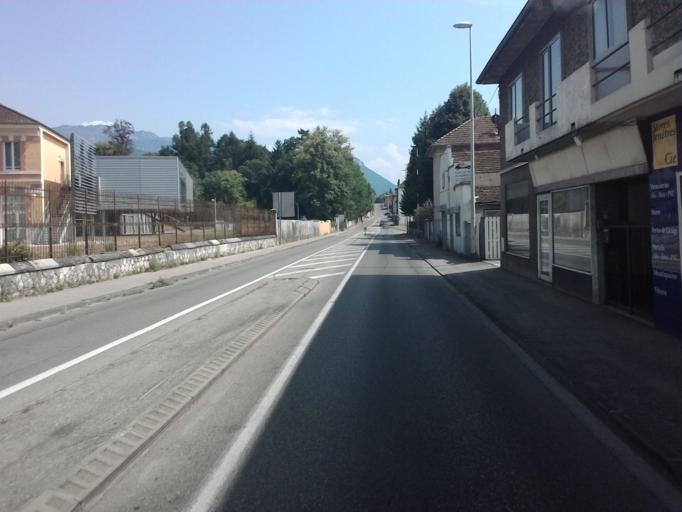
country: FR
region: Rhone-Alpes
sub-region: Departement de l'Isere
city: Voiron
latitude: 45.3608
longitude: 5.5994
